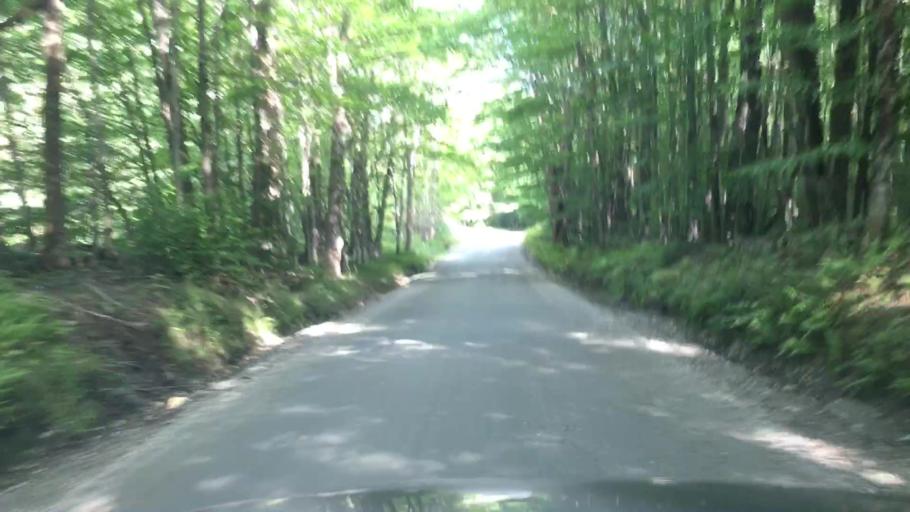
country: US
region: Vermont
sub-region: Windham County
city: Dover
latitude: 42.8221
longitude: -72.7701
